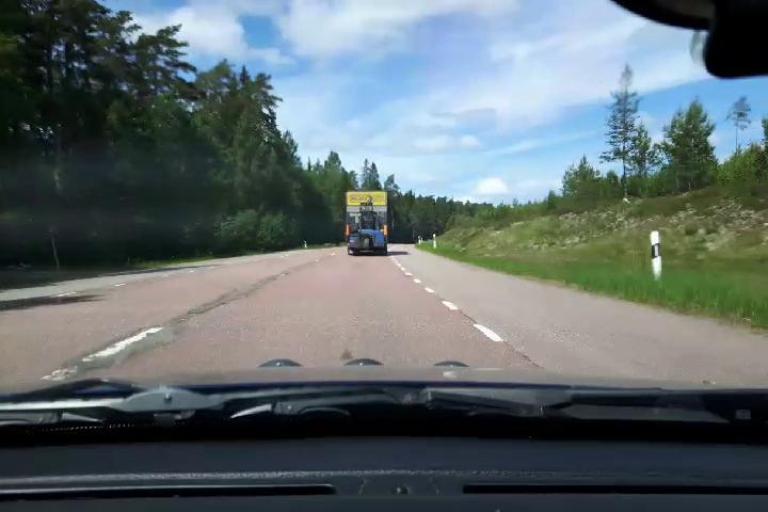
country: SE
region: Uppsala
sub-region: Osthammars Kommun
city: Bjorklinge
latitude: 60.1226
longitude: 17.5099
